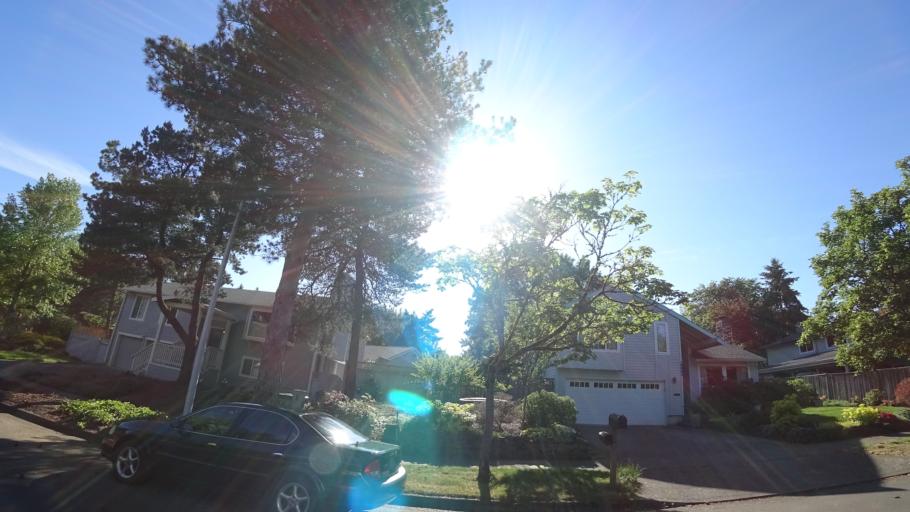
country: US
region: Oregon
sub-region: Washington County
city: Beaverton
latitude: 45.4556
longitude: -122.8091
